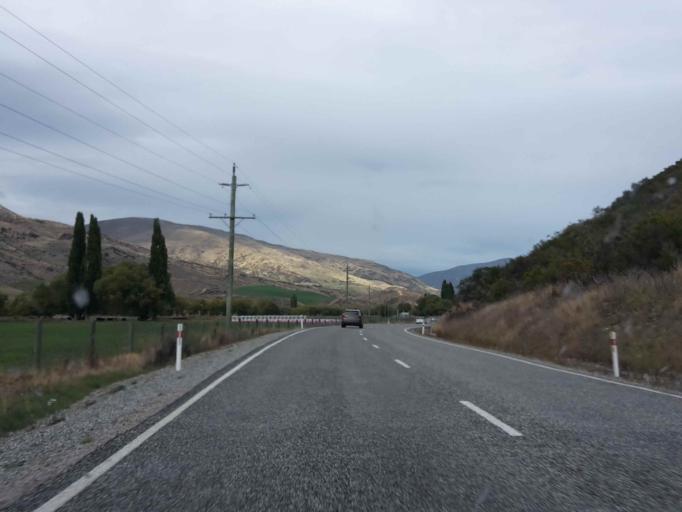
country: NZ
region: Otago
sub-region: Queenstown-Lakes District
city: Wanaka
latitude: -44.8434
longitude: 169.0478
